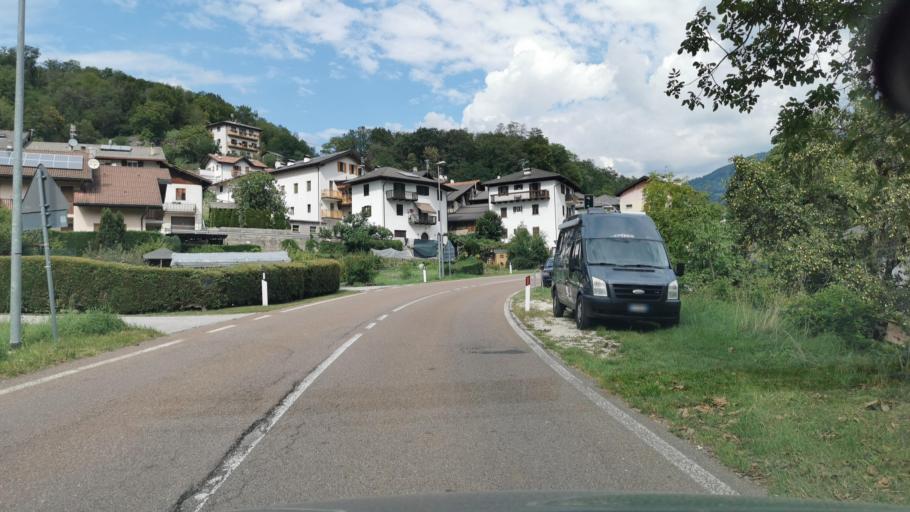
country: IT
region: Trentino-Alto Adige
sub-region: Provincia di Trento
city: Frassilongo
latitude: 46.0795
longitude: 11.2746
